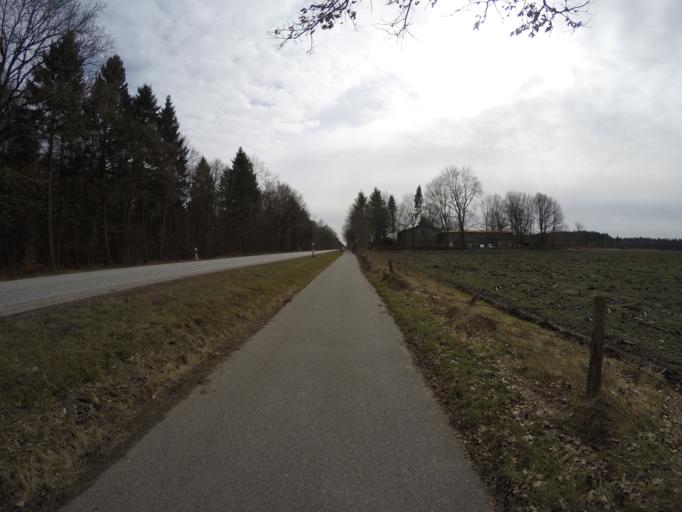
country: DE
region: Schleswig-Holstein
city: Heidmoor
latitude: 53.8283
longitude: 9.8832
